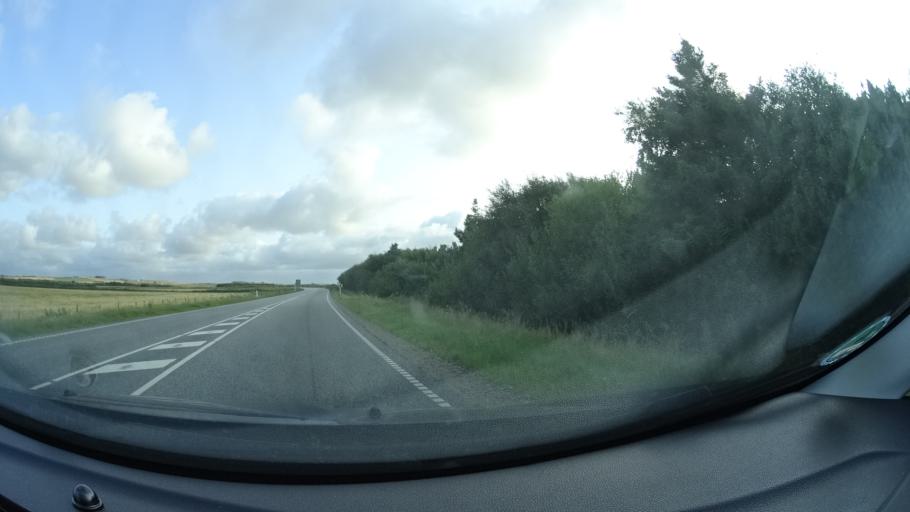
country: DK
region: Central Jutland
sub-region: Lemvig Kommune
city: Harboore
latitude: 56.6092
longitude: 8.1836
